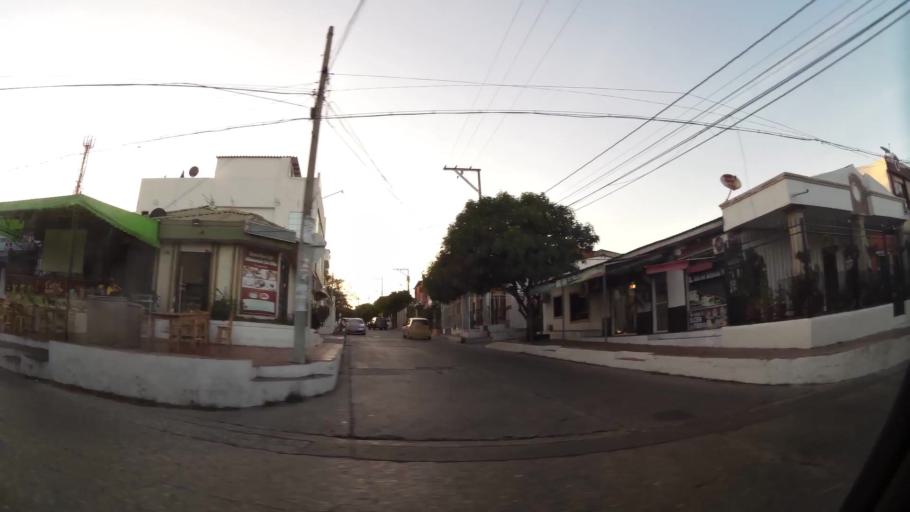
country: CO
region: Atlantico
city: Barranquilla
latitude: 10.9761
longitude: -74.8071
